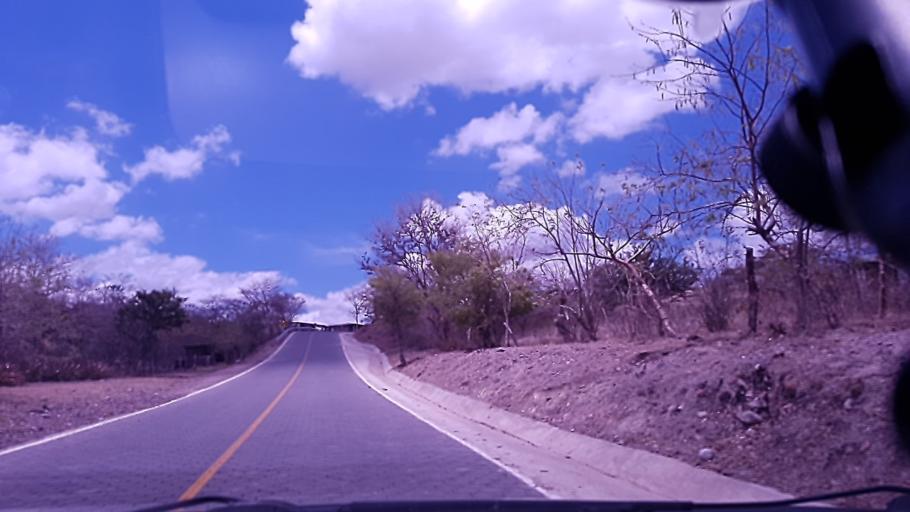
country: NI
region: Esteli
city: Condega
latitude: 13.3718
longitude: -86.3774
